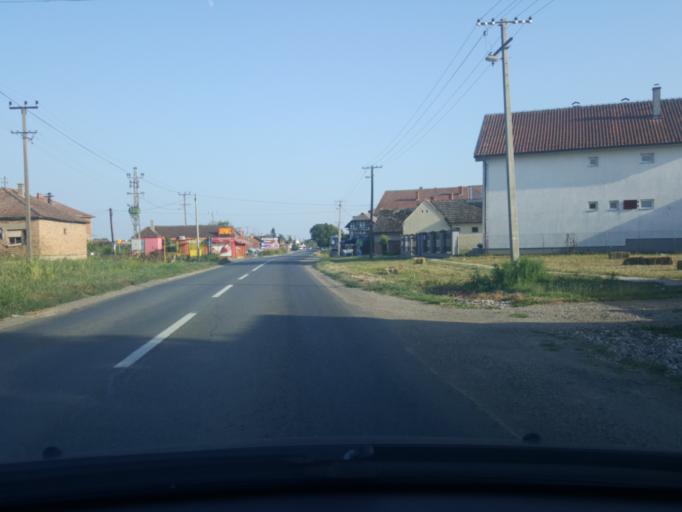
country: RS
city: Platicevo
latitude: 44.8276
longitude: 19.7785
